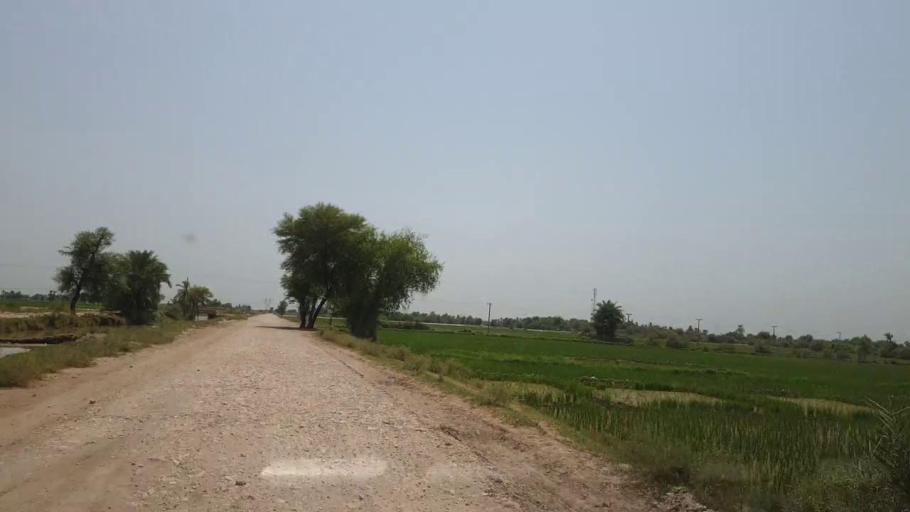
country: PK
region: Sindh
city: Lakhi
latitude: 27.8655
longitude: 68.6066
